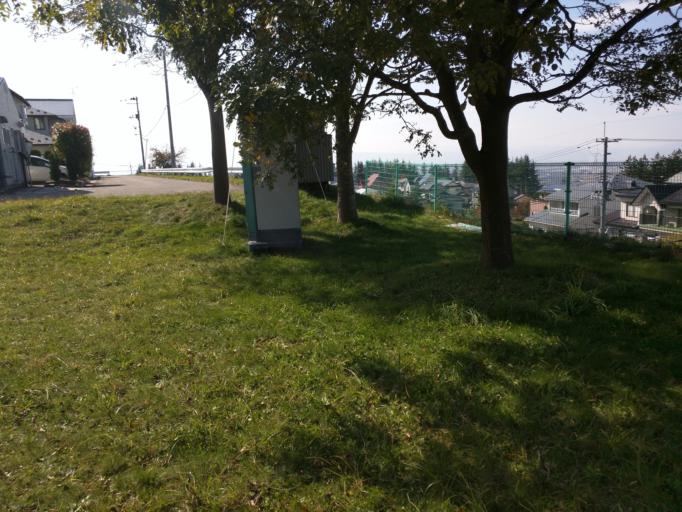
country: JP
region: Fukushima
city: Kitakata
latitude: 37.5285
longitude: 139.9560
